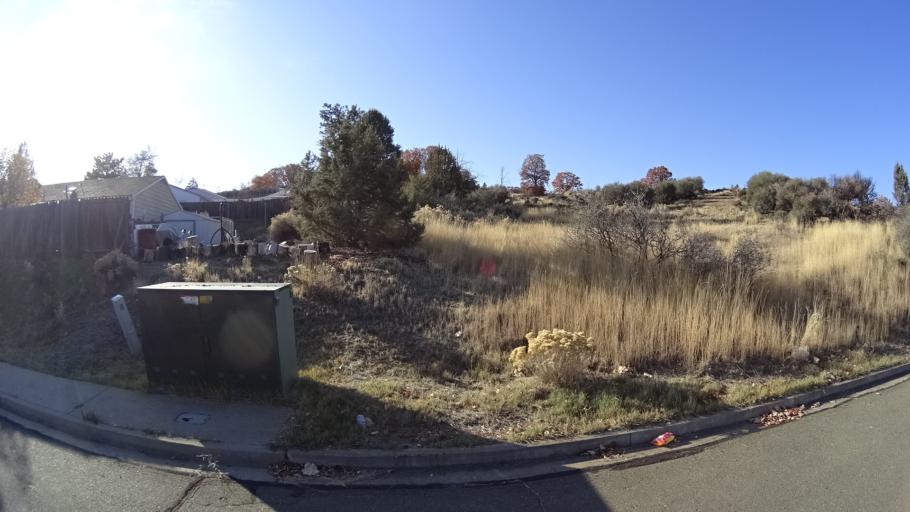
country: US
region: California
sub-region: Siskiyou County
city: Yreka
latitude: 41.7108
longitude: -122.6249
